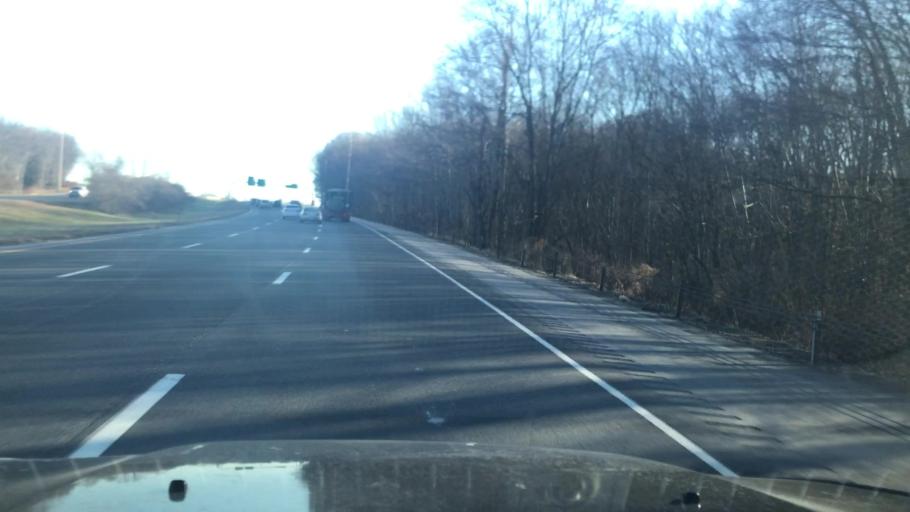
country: US
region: Connecticut
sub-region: New Haven County
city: Wolcott
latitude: 41.5912
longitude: -72.9028
